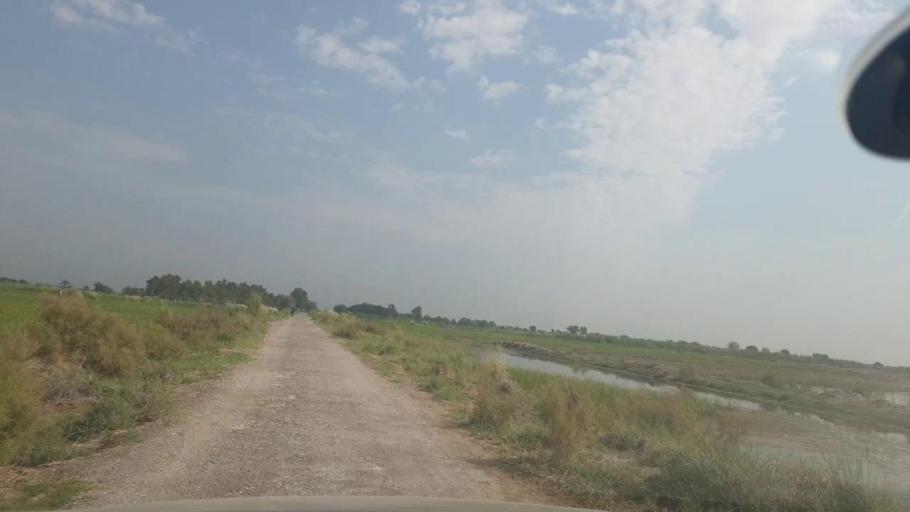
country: PK
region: Balochistan
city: Mehrabpur
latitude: 28.0487
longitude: 68.1226
